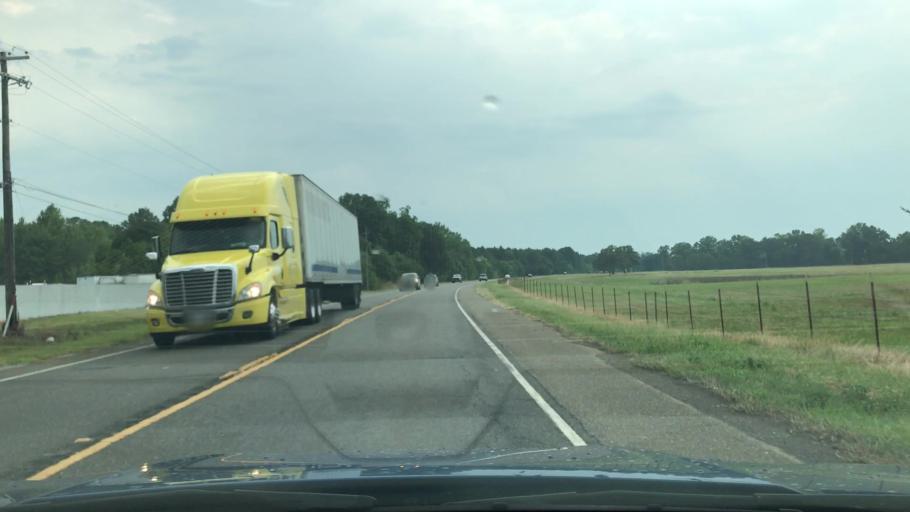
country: US
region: Texas
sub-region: Harrison County
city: Waskom
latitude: 32.4605
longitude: -94.0255
